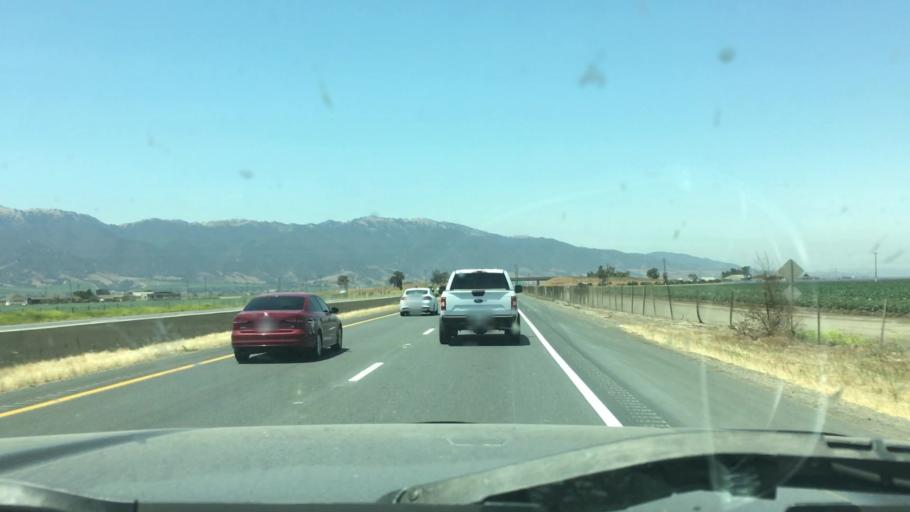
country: US
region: California
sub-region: Monterey County
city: Gonzales
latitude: 36.5230
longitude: -121.4566
